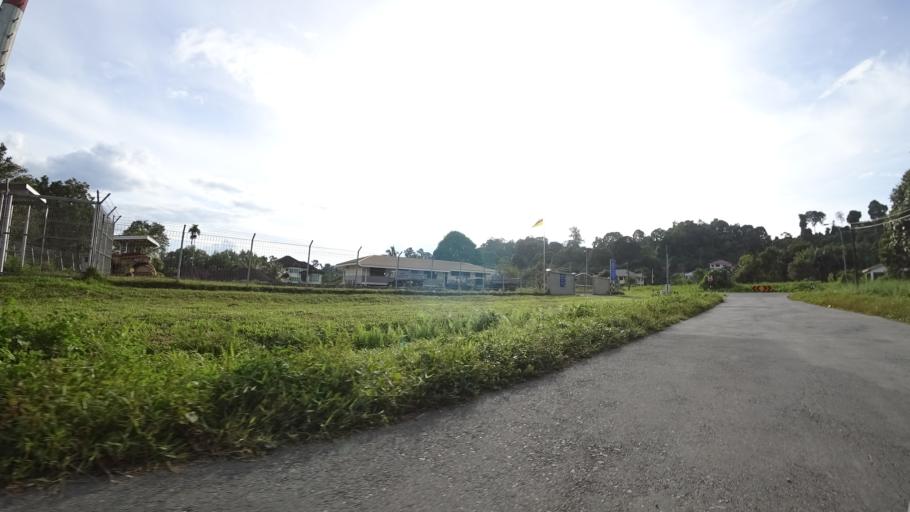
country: BN
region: Tutong
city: Tutong
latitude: 4.8176
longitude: 114.8169
